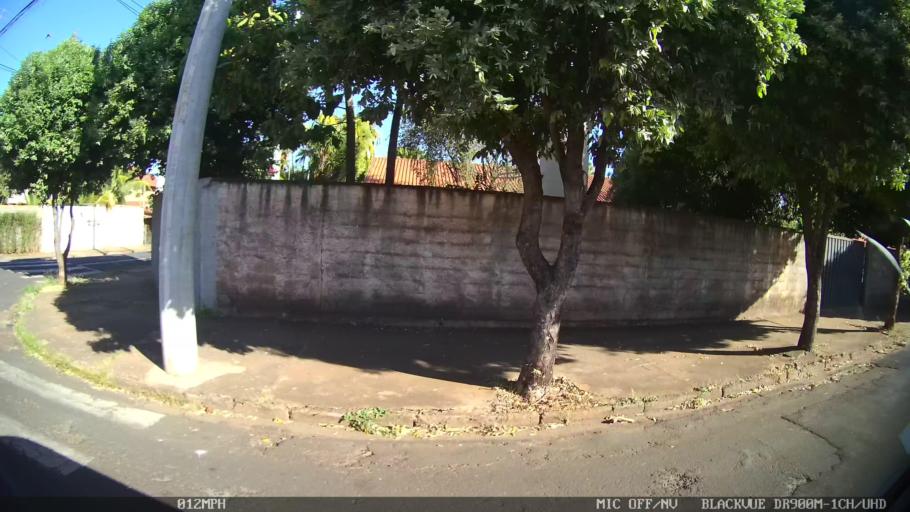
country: BR
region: Sao Paulo
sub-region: Olimpia
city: Olimpia
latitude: -20.7402
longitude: -48.8962
